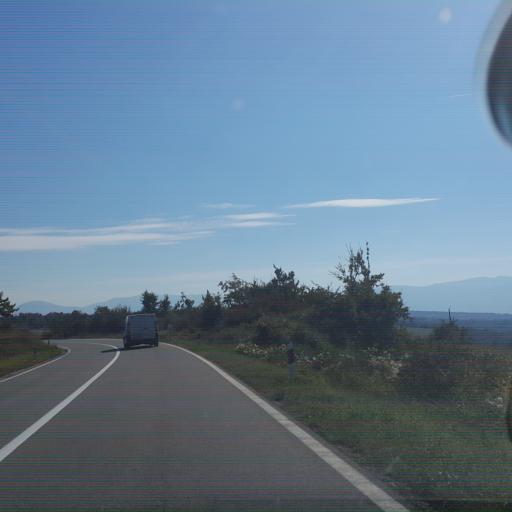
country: RS
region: Central Serbia
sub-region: Zajecarski Okrug
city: Knjazevac
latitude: 43.4841
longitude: 22.2283
